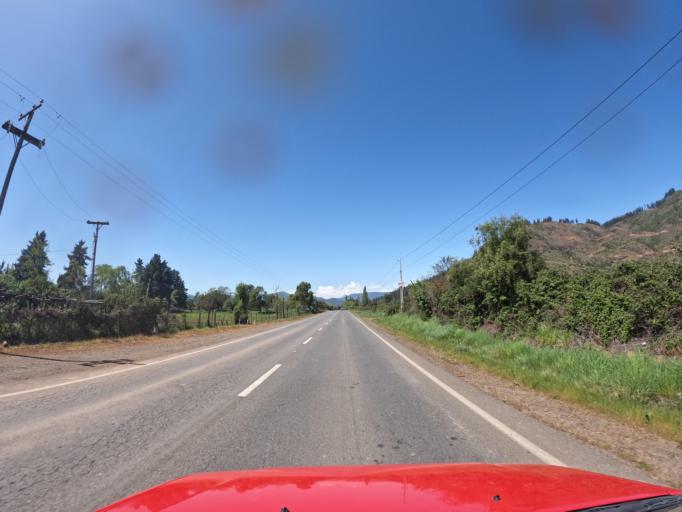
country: CL
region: Maule
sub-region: Provincia de Talca
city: San Clemente
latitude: -35.4849
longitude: -71.2755
